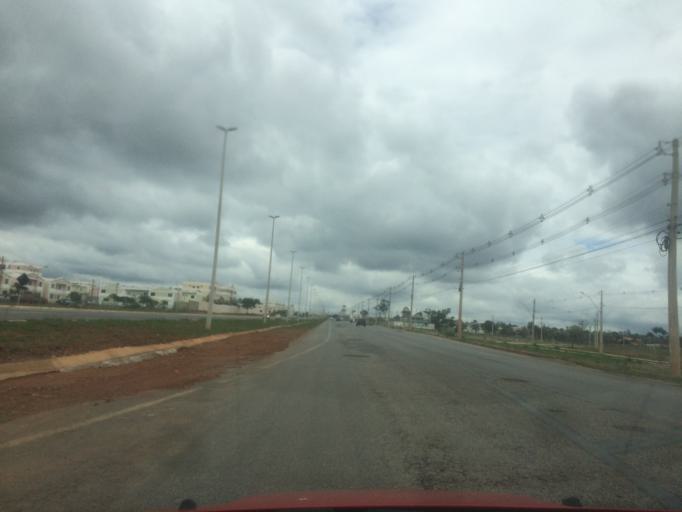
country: BR
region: Federal District
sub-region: Brasilia
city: Brasilia
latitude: -15.8877
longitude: -47.8080
